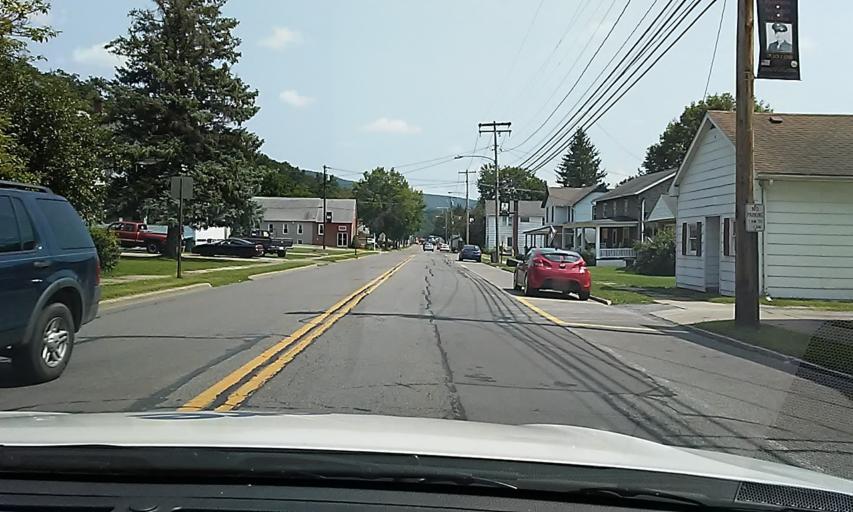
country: US
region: Pennsylvania
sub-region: Cameron County
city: Emporium
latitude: 41.5118
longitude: -78.2296
